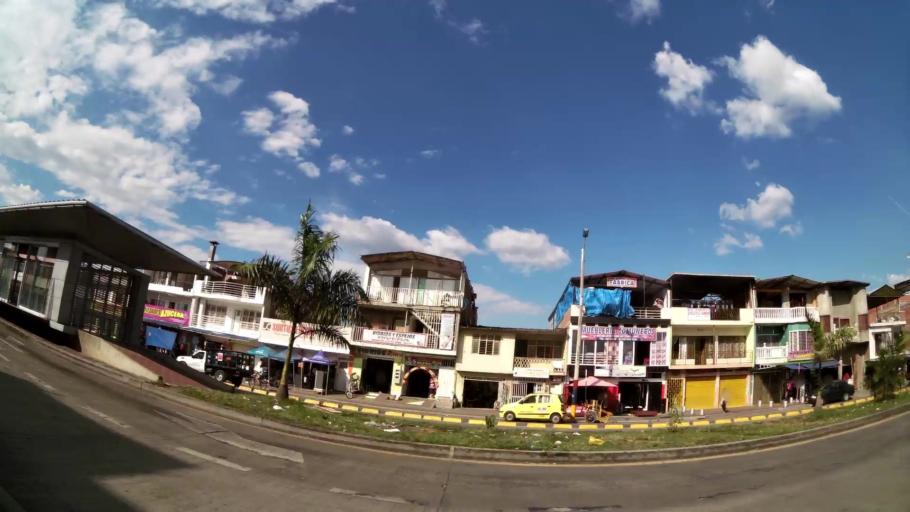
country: CO
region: Valle del Cauca
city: Cali
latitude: 3.4246
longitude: -76.4942
